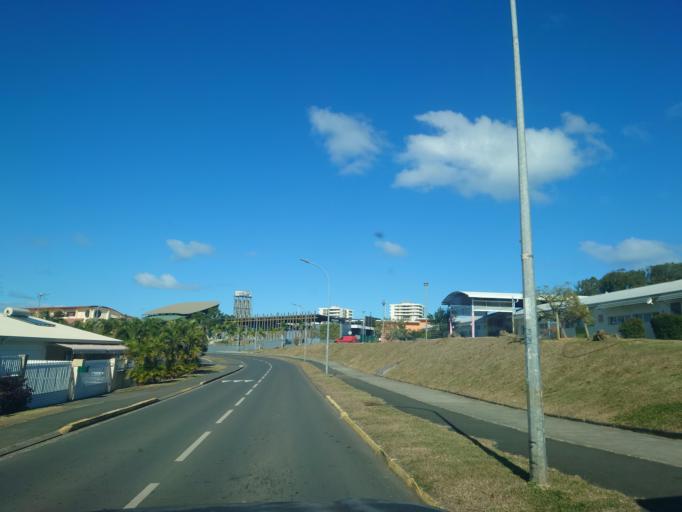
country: NC
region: South Province
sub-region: Noumea
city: Noumea
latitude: -22.2682
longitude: 166.4692
